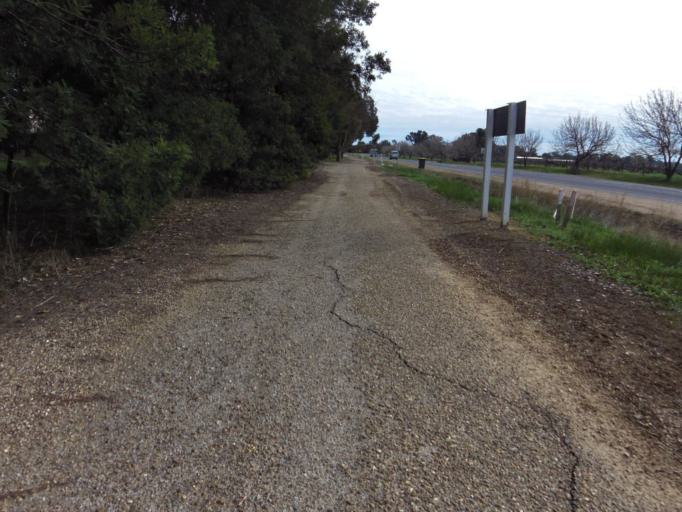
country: AU
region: Victoria
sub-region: Wangaratta
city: Wangaratta
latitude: -36.4383
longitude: 146.3595
